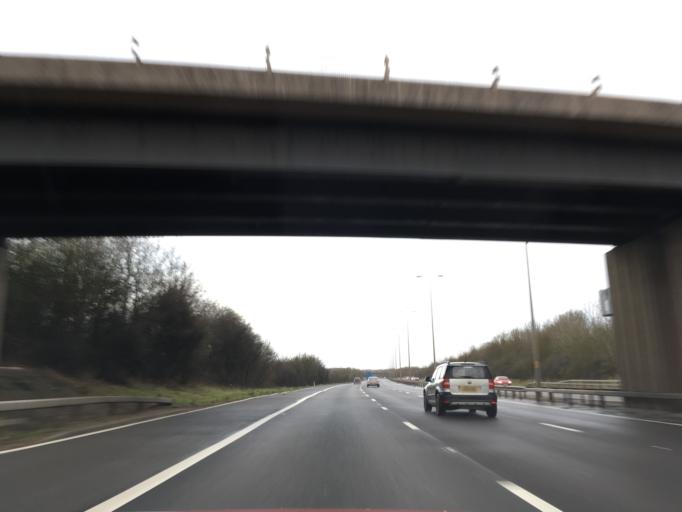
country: GB
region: England
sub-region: Worcestershire
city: Kempsey
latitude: 52.1323
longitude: -2.2005
